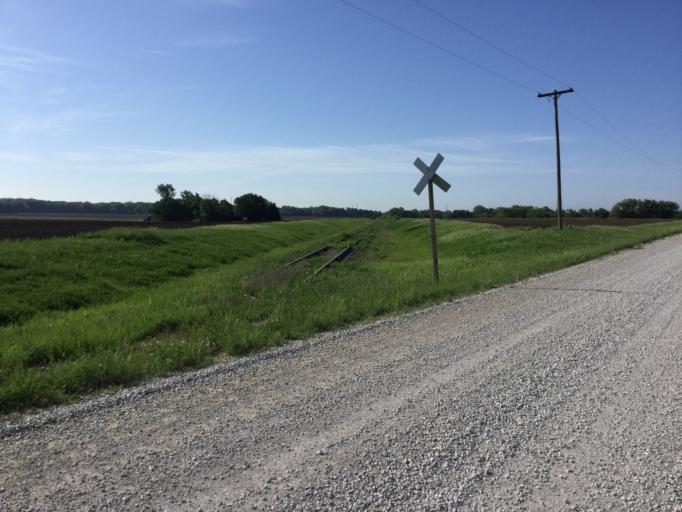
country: US
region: Kansas
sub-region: Coffey County
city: Burlington
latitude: 38.2163
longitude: -95.6472
